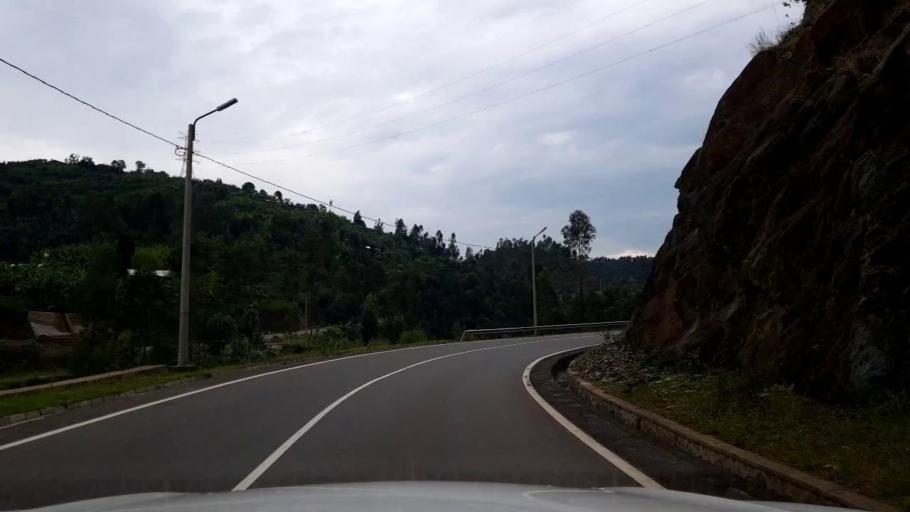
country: RW
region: Western Province
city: Kibuye
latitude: -2.0308
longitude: 29.3984
